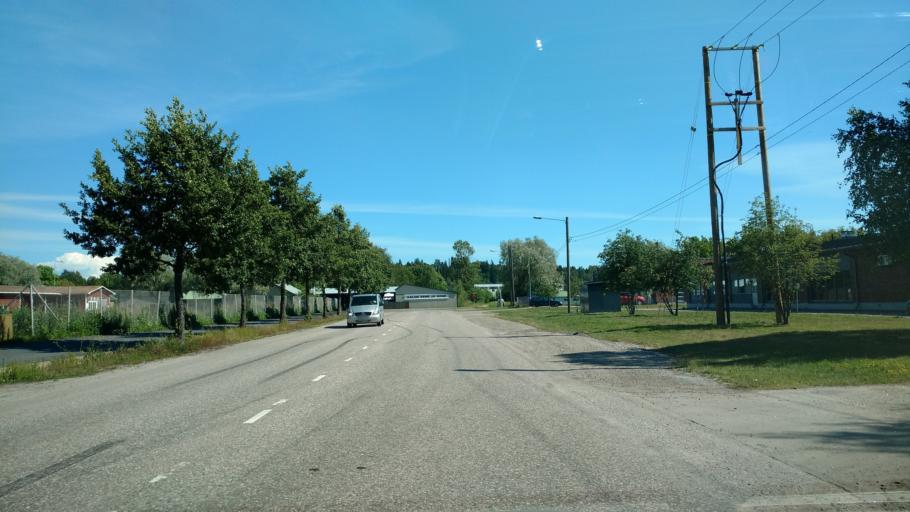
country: FI
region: Varsinais-Suomi
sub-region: Salo
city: Salo
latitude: 60.3810
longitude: 23.1148
